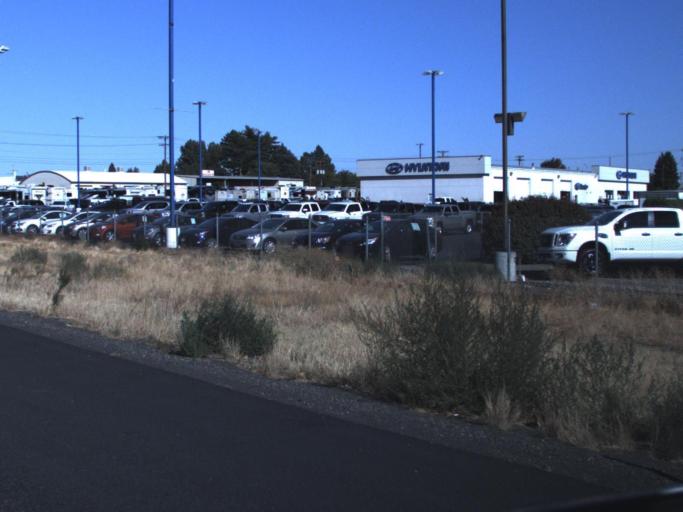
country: US
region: Washington
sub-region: Benton County
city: Kennewick
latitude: 46.2369
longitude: -119.1306
